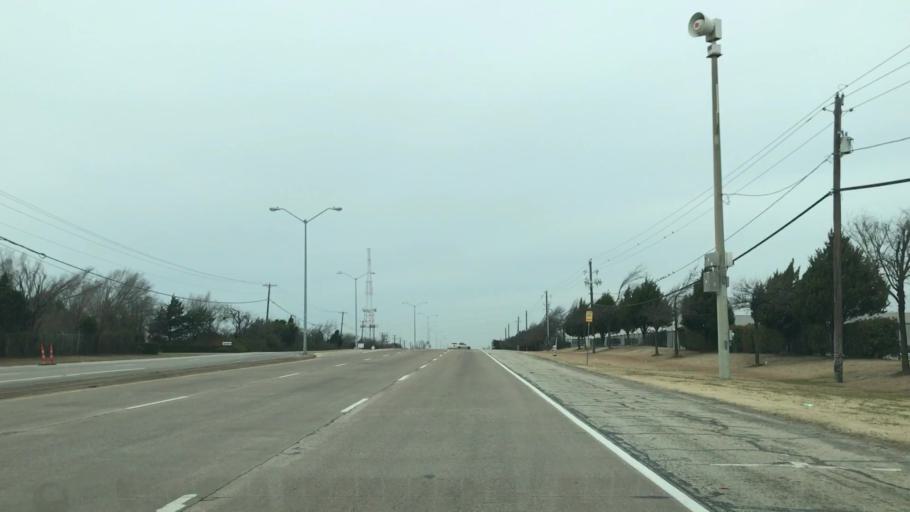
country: US
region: Texas
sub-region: Dallas County
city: Cockrell Hill
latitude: 32.7498
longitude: -96.8918
